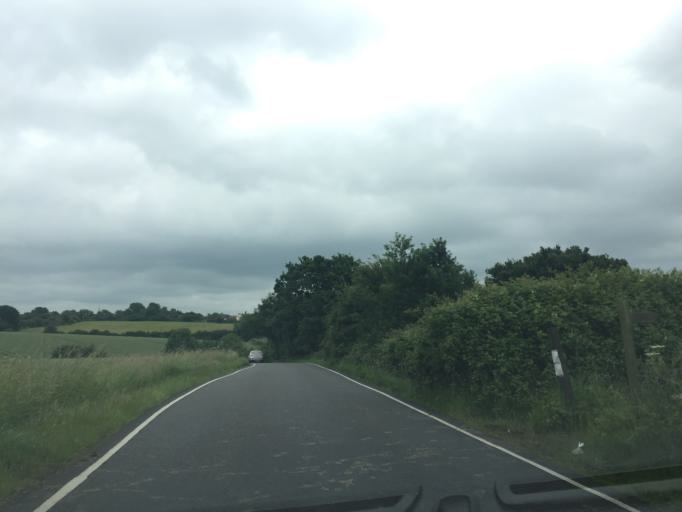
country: GB
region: England
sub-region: Essex
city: Harlow
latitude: 51.7375
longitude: 0.1062
